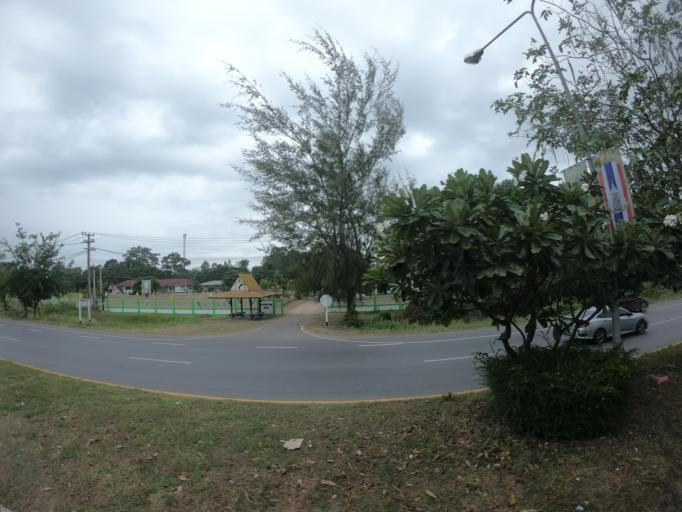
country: TH
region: Maha Sarakham
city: Maha Sarakham
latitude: 16.1657
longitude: 103.2861
